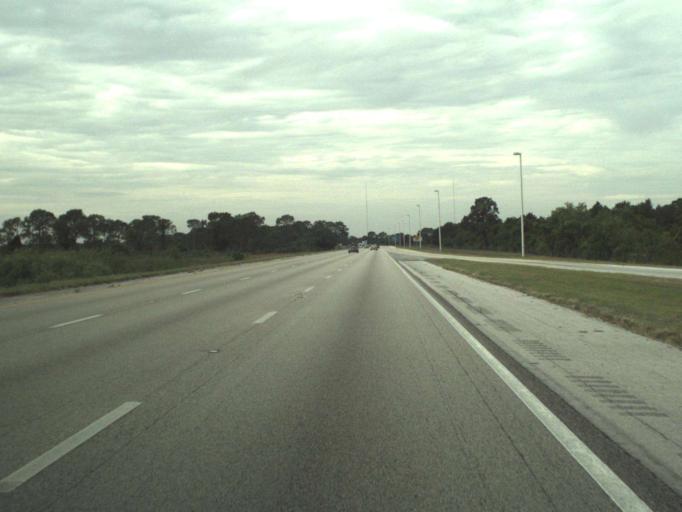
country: US
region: Florida
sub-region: Saint Lucie County
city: Port Saint Lucie
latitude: 27.1851
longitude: -80.3991
